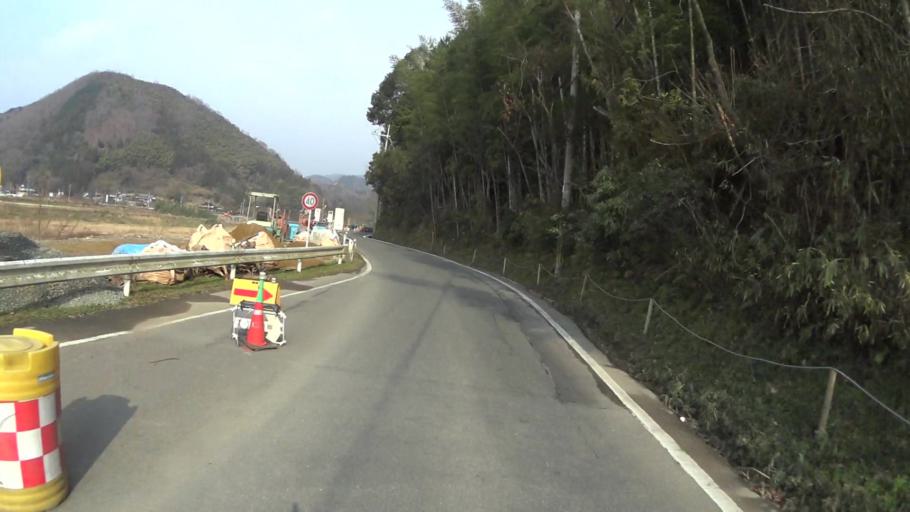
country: JP
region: Kyoto
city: Fukuchiyama
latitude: 35.3562
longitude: 135.1167
